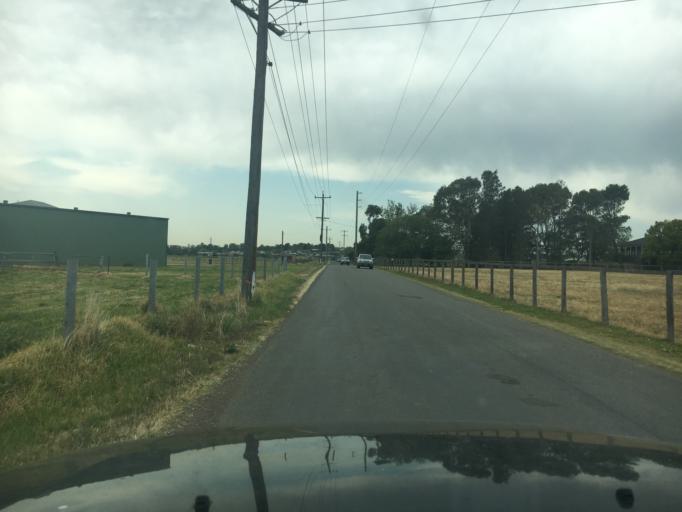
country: AU
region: New South Wales
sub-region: Maitland Municipality
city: Lorn
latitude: -32.7509
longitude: 151.5633
